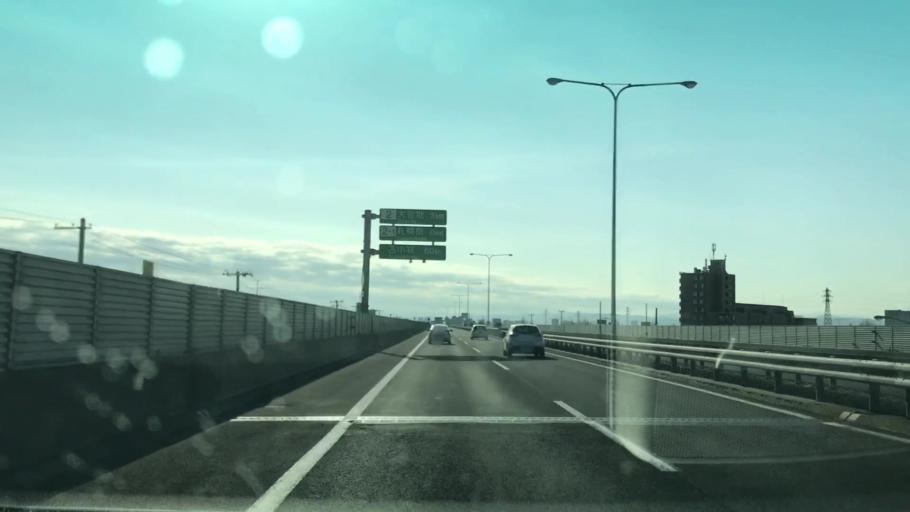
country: JP
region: Hokkaido
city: Sapporo
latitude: 43.0656
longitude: 141.4235
